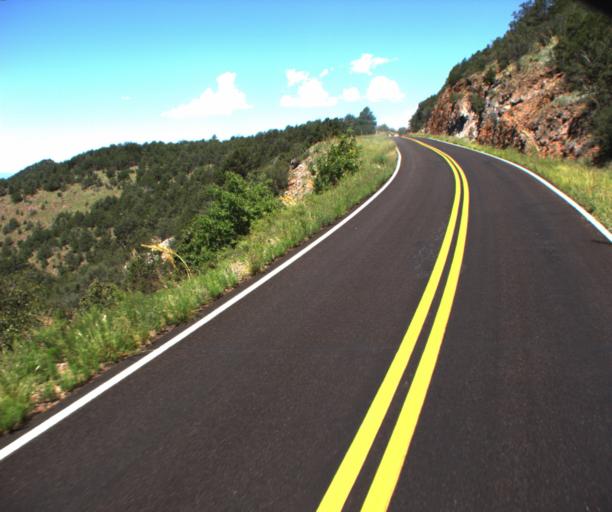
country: US
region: Arizona
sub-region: Greenlee County
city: Morenci
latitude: 33.4132
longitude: -109.3670
